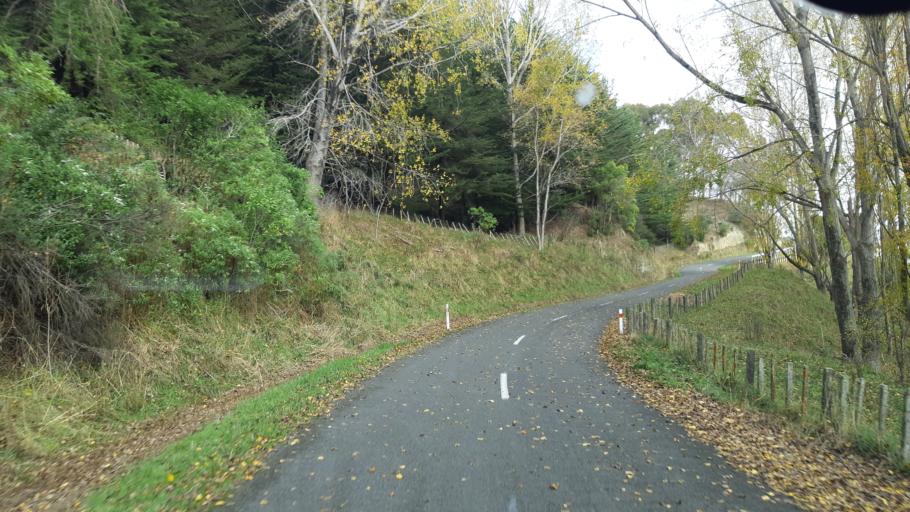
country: NZ
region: Manawatu-Wanganui
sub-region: Ruapehu District
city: Waiouru
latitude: -39.7259
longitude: 175.6727
